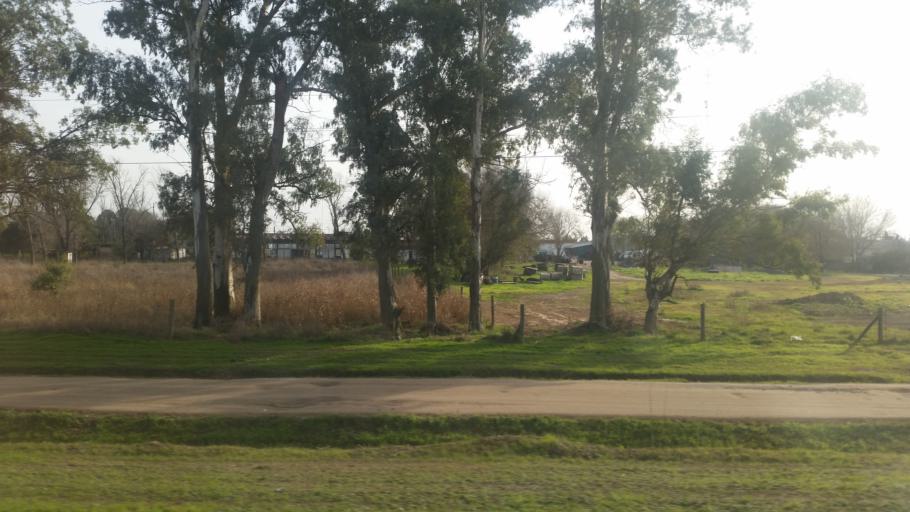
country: AR
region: Cordoba
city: Bell Ville
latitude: -32.6104
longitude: -62.6833
